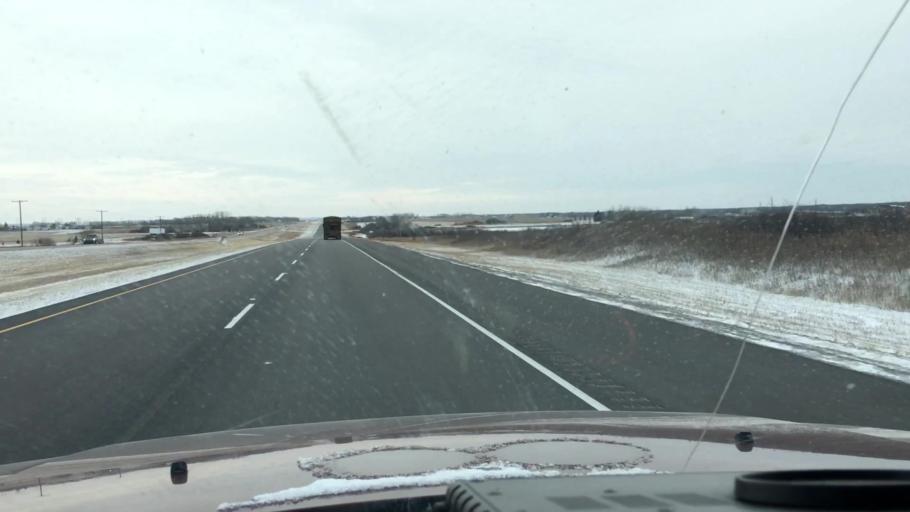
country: CA
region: Saskatchewan
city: Saskatoon
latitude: 51.9264
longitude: -106.5337
